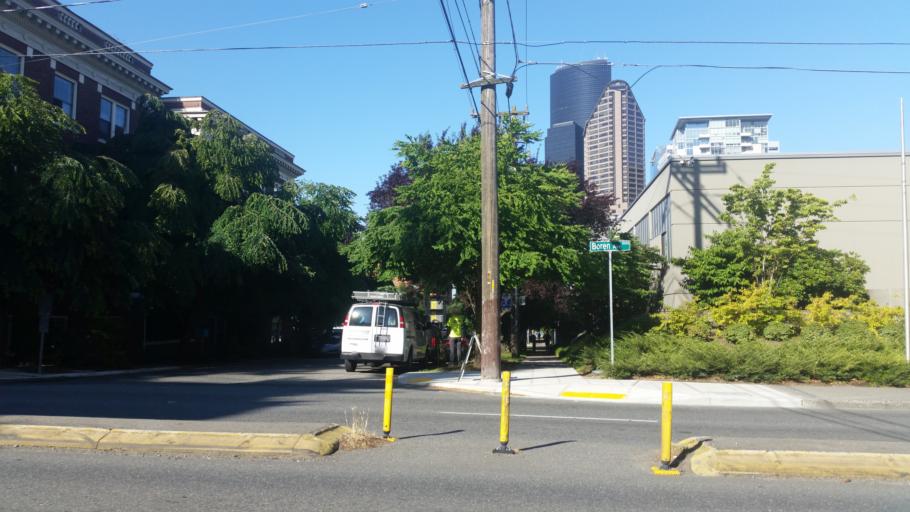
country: US
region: Washington
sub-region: King County
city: Seattle
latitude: 47.6073
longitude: -122.3232
